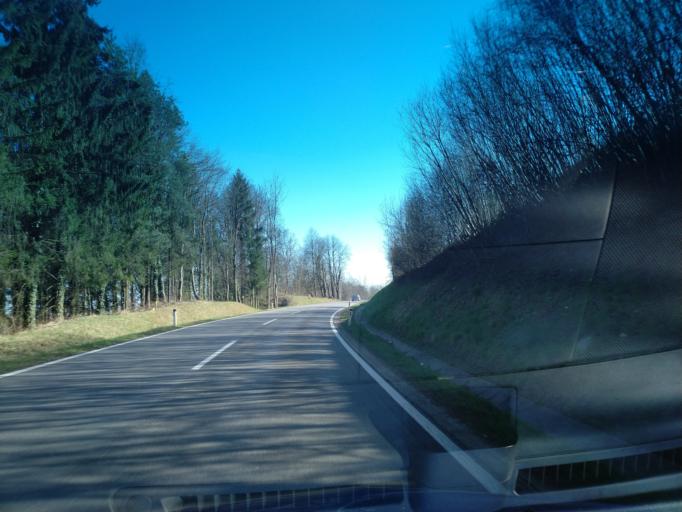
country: AT
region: Styria
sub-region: Politischer Bezirk Leibnitz
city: Stocking
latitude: 46.8729
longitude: 15.5301
